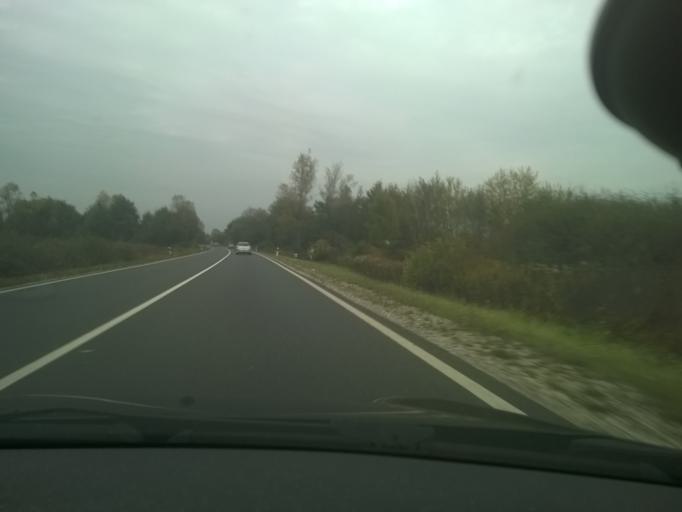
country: HR
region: Zagrebacka
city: Jakovlje
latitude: 45.9668
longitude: 15.8463
